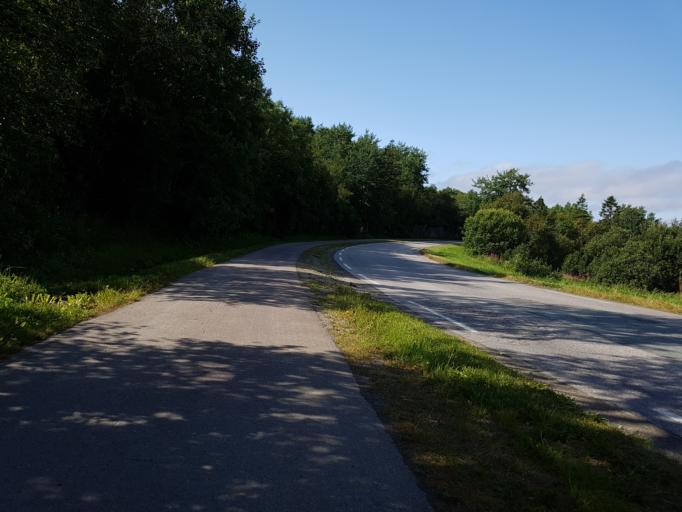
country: NO
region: Sor-Trondelag
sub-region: Agdenes
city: Lensvik
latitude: 63.6350
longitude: 9.8375
